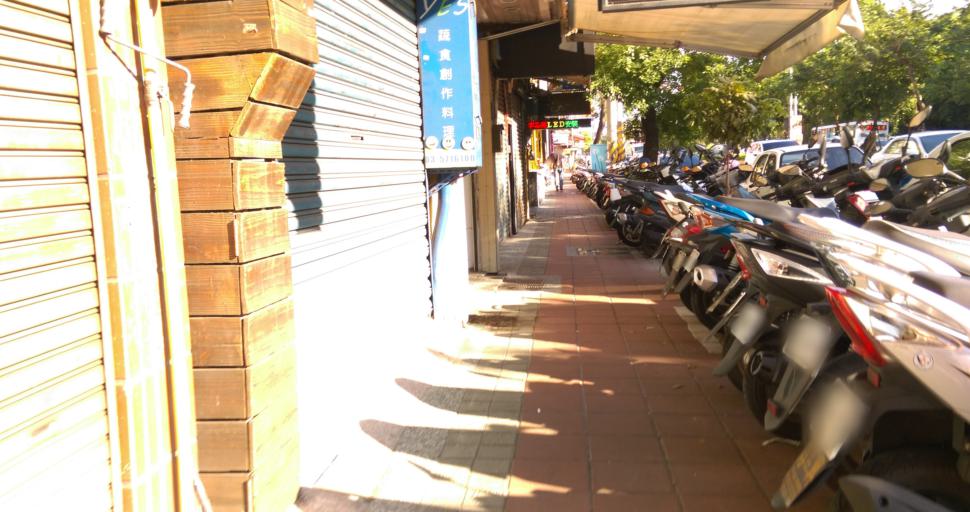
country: TW
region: Taiwan
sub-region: Hsinchu
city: Hsinchu
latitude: 24.7944
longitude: 121.0001
